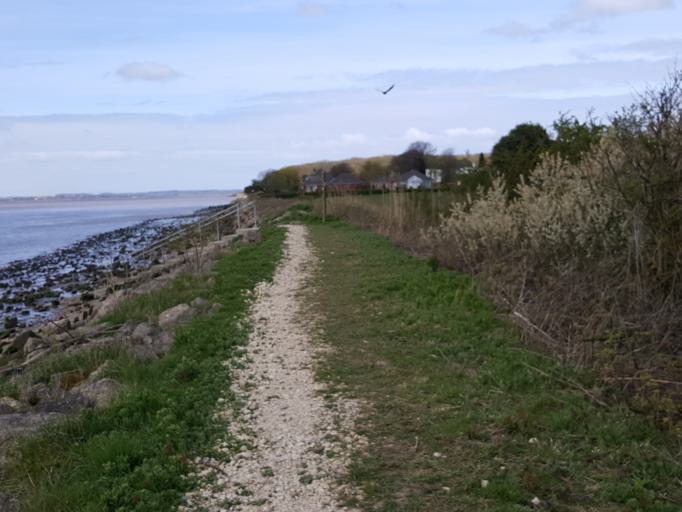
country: GB
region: England
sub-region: East Riding of Yorkshire
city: North Ferriby
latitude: 53.7142
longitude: -0.5024
